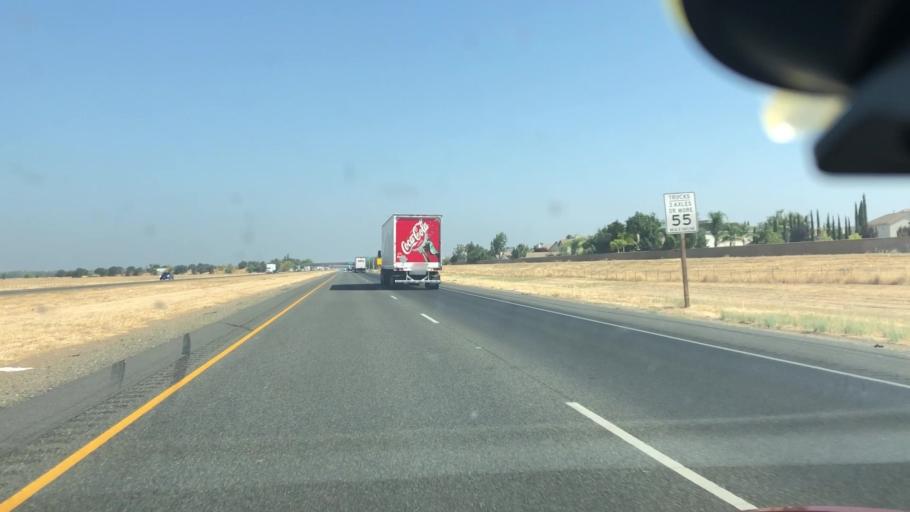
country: US
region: California
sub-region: Sacramento County
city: Laguna
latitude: 38.4004
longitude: -121.4821
